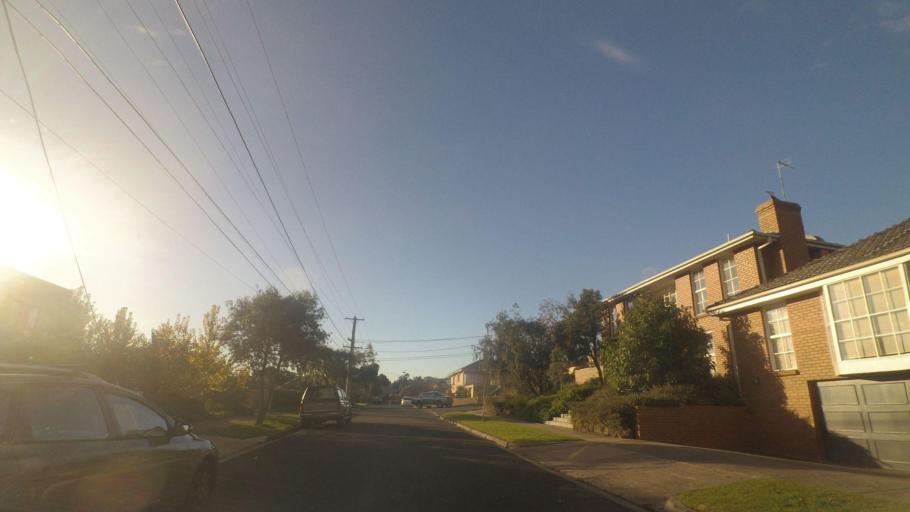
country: AU
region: Victoria
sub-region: Boroondara
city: Balwyn North
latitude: -37.7771
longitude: 145.0993
